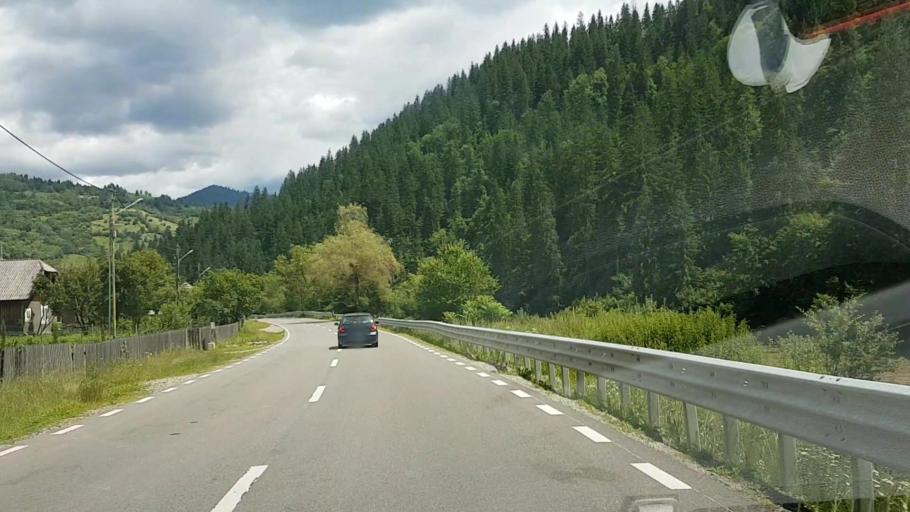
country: RO
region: Suceava
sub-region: Comuna Brosteni
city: Brosteni
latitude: 47.2560
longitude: 25.6730
